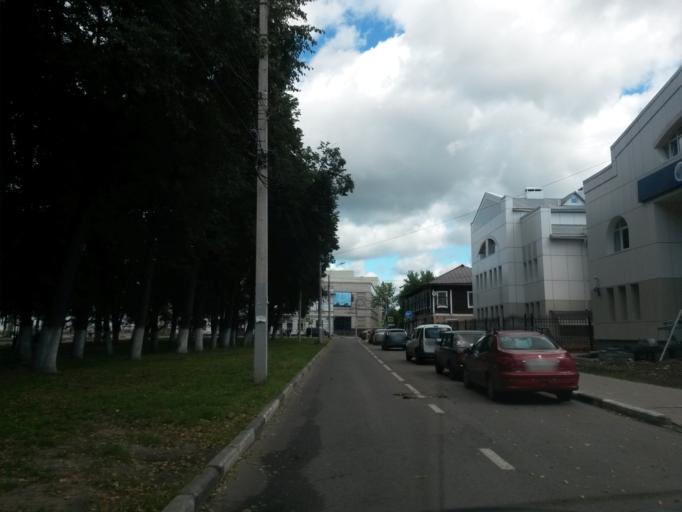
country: RU
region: Jaroslavl
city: Yaroslavl
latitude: 57.6247
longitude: 39.8719
